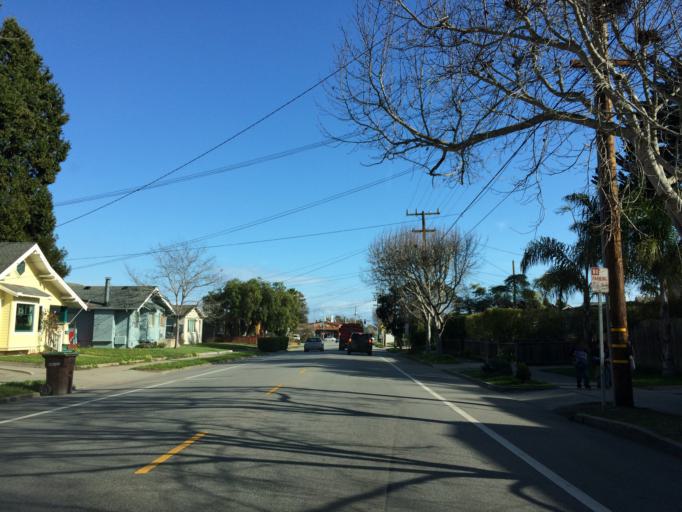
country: US
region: California
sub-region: Santa Cruz County
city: Santa Cruz
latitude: 36.9676
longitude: -122.0421
